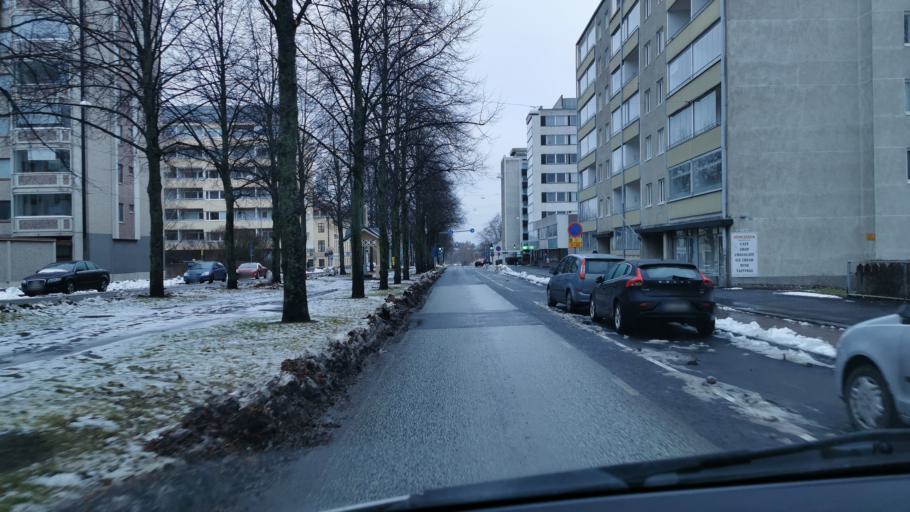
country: FI
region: Ostrobothnia
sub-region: Vaasa
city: Vaasa
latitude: 63.0986
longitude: 21.6068
